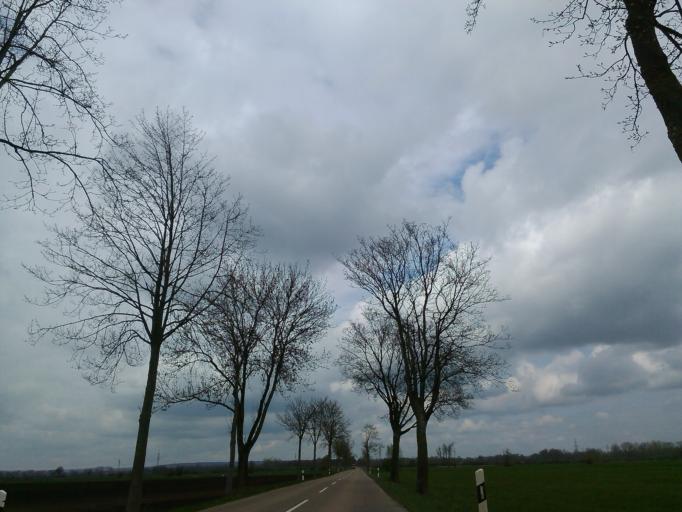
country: DE
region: Baden-Wuerttemberg
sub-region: Tuebingen Region
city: Rammingen
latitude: 48.4636
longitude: 10.1682
